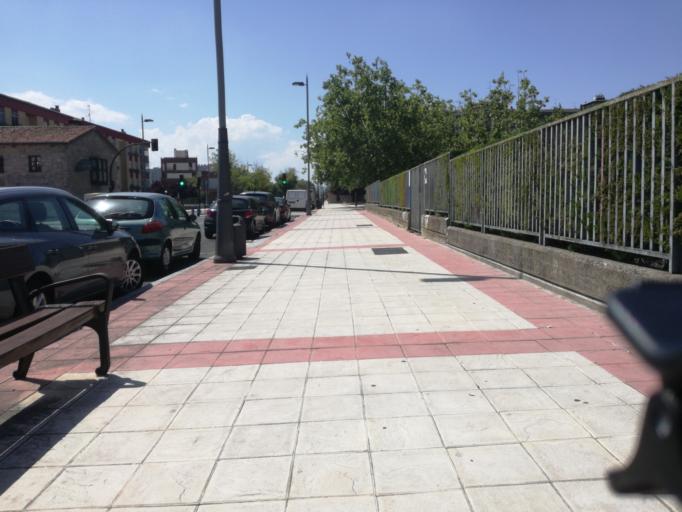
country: ES
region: Basque Country
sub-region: Provincia de Alava
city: Gasteiz / Vitoria
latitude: 42.8541
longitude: -2.7008
